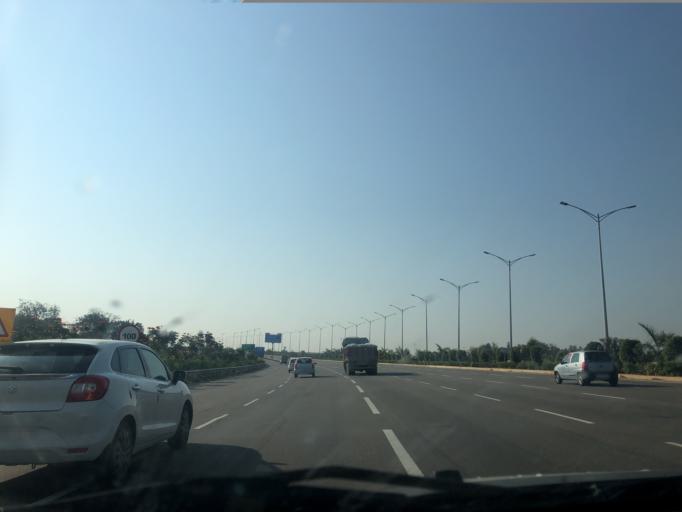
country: IN
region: Telangana
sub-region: Rangareddi
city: Sriramnagar
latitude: 17.2570
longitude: 78.3756
